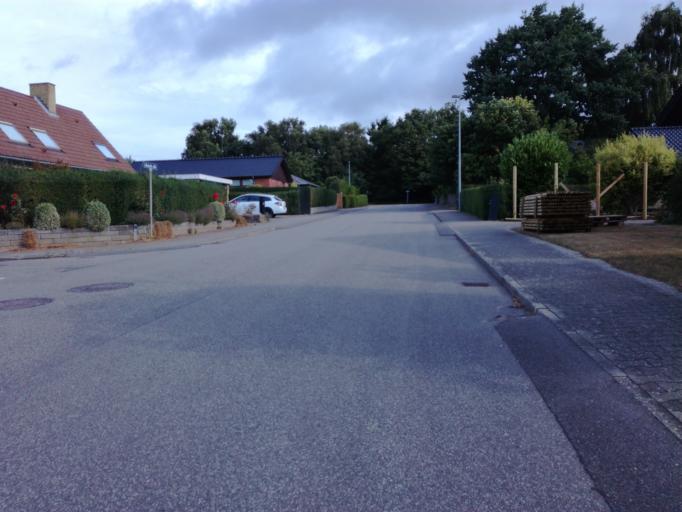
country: DK
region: South Denmark
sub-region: Fredericia Kommune
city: Fredericia
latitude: 55.5820
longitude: 9.7857
